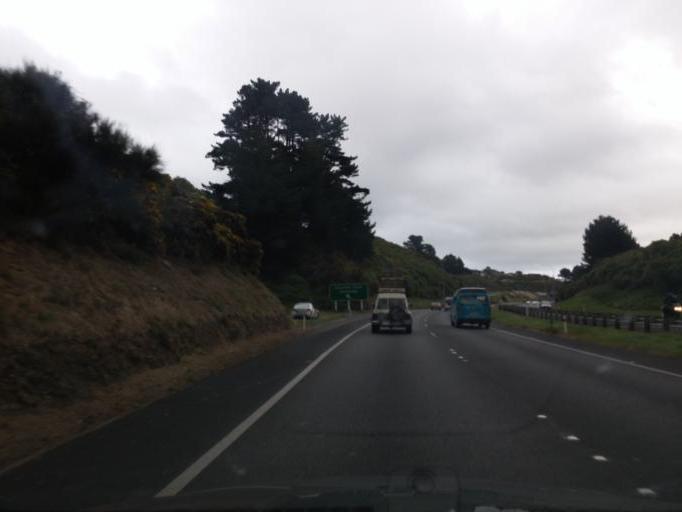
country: NZ
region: Wellington
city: Petone
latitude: -41.1995
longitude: 174.8241
